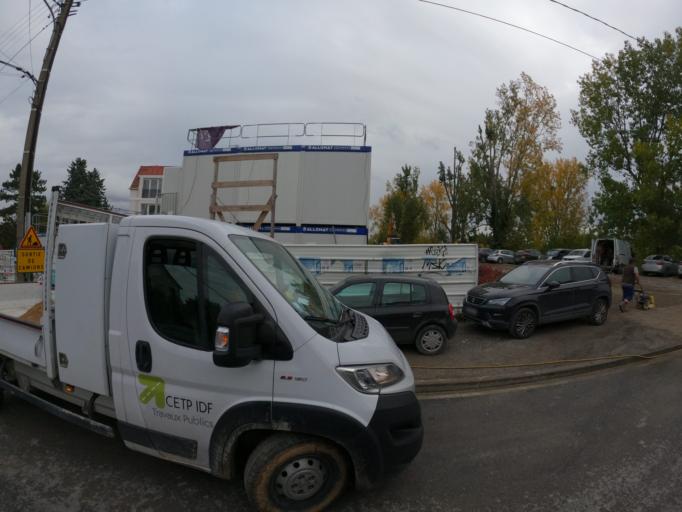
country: FR
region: Ile-de-France
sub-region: Departement de Seine-Saint-Denis
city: Gournay-sur-Marne
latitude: 48.8682
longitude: 2.5879
